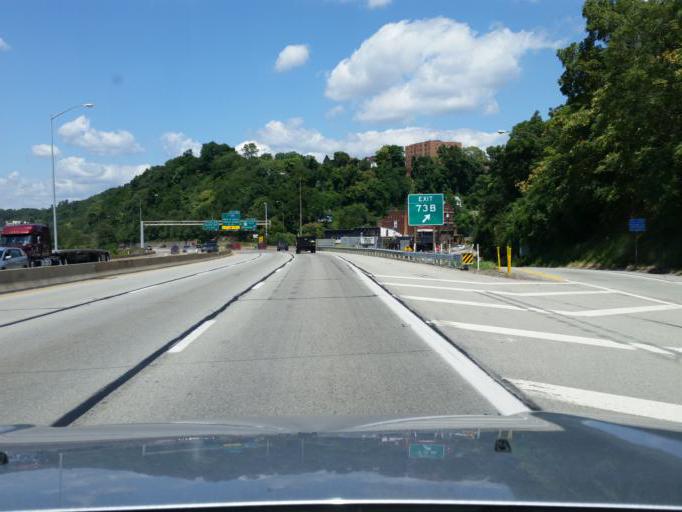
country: US
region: Pennsylvania
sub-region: Allegheny County
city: Bloomfield
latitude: 40.4304
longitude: -79.9575
